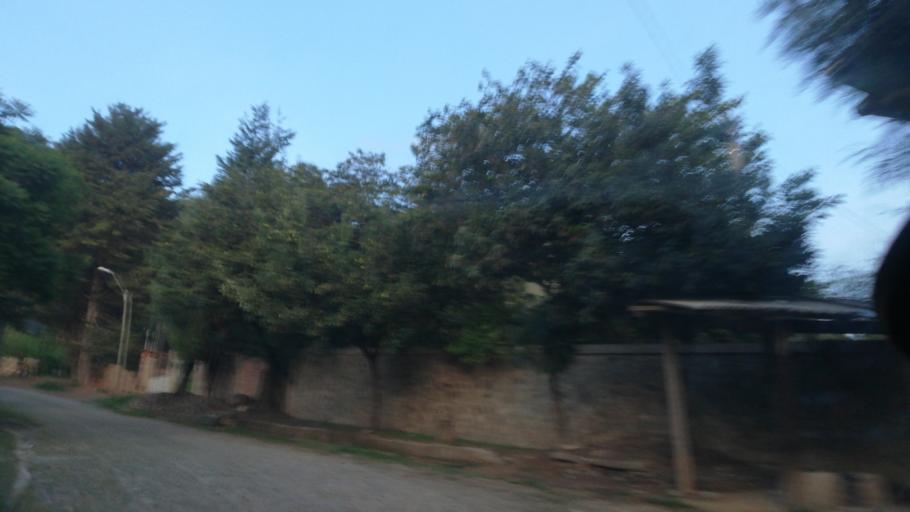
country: BO
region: Cochabamba
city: Cochabamba
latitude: -17.3207
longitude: -66.2077
